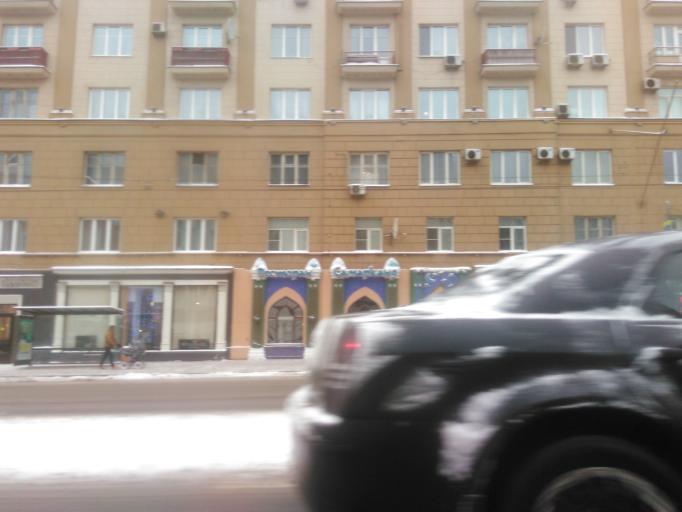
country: RU
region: Moscow
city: Mar'ina Roshcha
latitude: 55.7818
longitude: 37.6337
